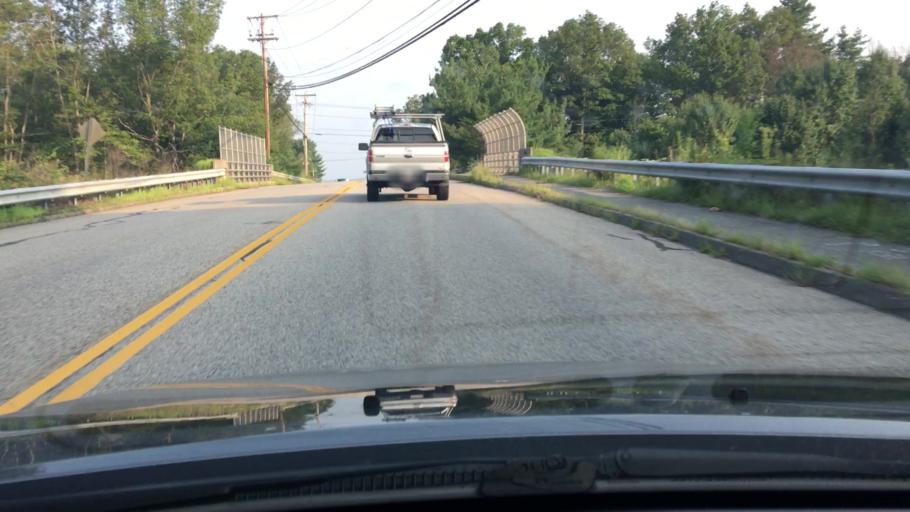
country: US
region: Massachusetts
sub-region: Worcester County
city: Westborough
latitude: 42.2705
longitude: -71.6413
